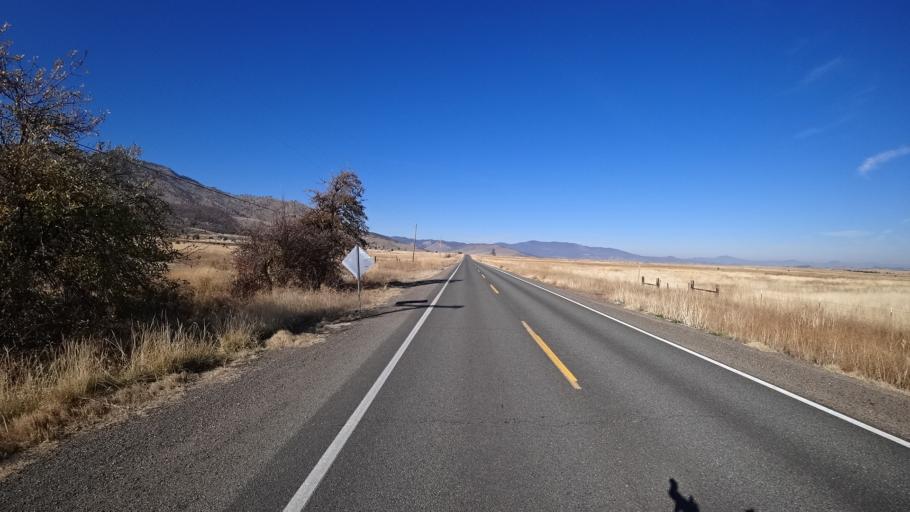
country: US
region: California
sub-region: Siskiyou County
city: Weed
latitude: 41.4708
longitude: -122.4779
